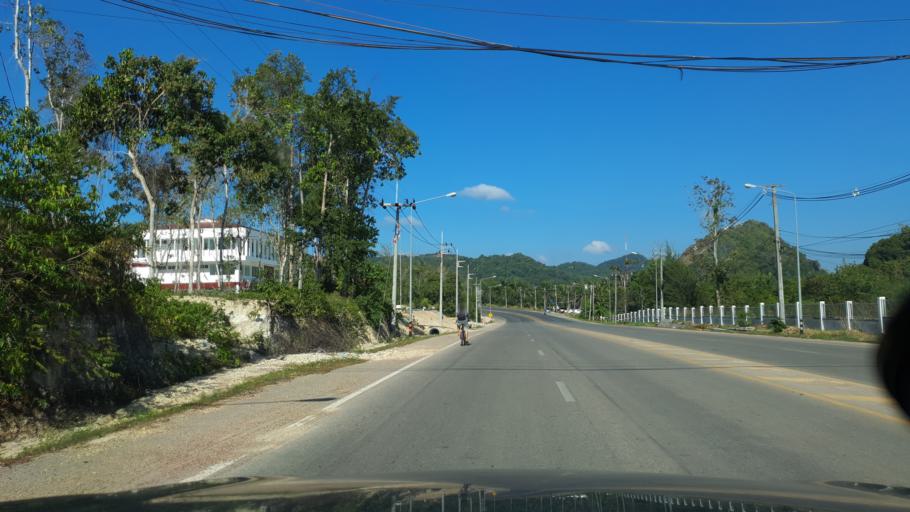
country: TH
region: Phangnga
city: Ban Ao Nang
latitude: 8.0405
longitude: 98.8497
